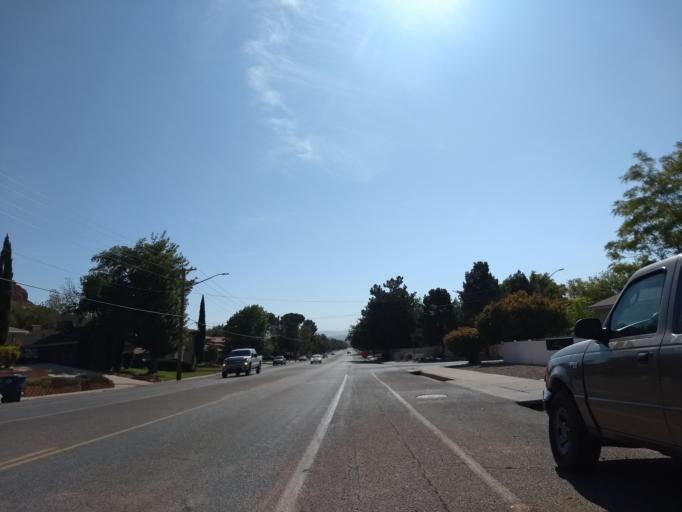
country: US
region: Utah
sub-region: Washington County
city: Saint George
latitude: 37.1207
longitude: -113.5963
